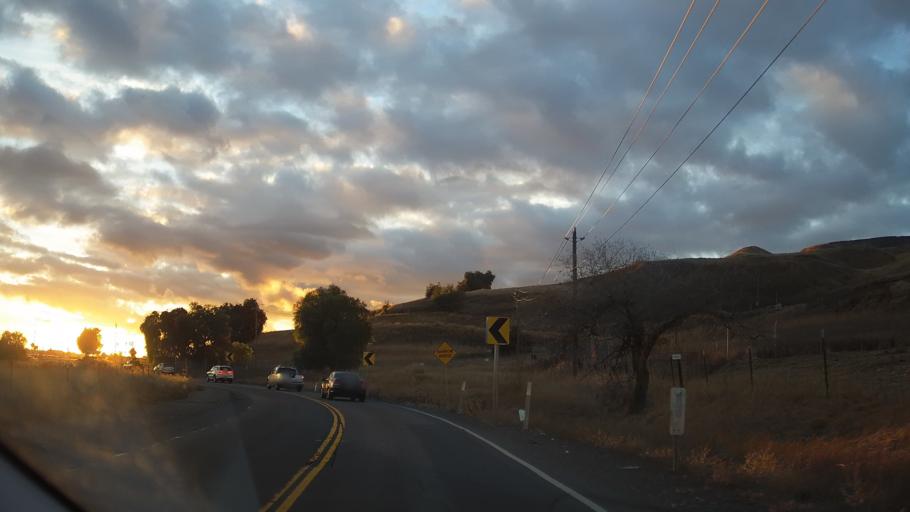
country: US
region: California
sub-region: Solano County
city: Fairfield
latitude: 38.2872
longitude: -121.9941
